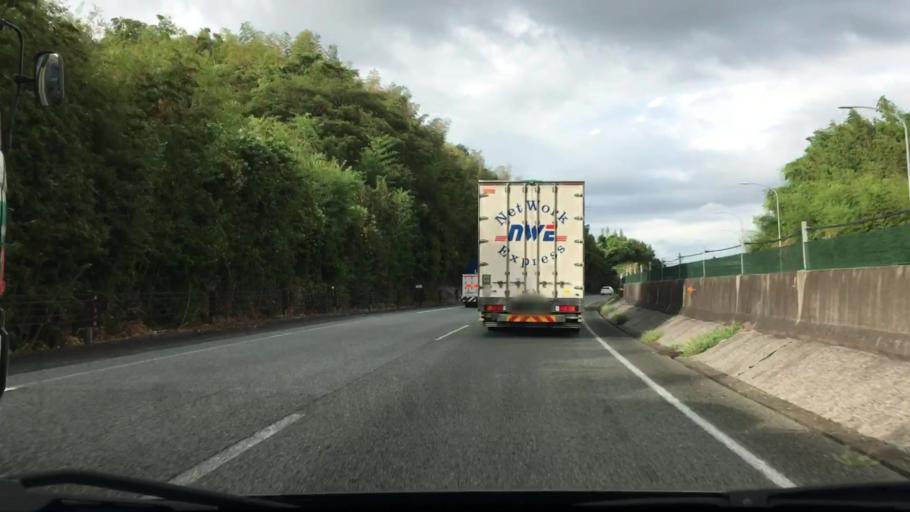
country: JP
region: Fukuoka
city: Nishifukuma
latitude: 33.7474
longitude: 130.5284
